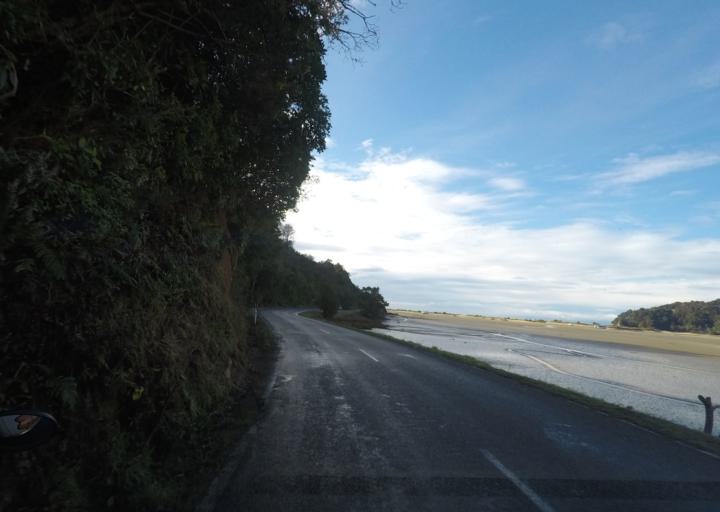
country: NZ
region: Tasman
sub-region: Tasman District
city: Motueka
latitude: -41.0123
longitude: 172.9997
